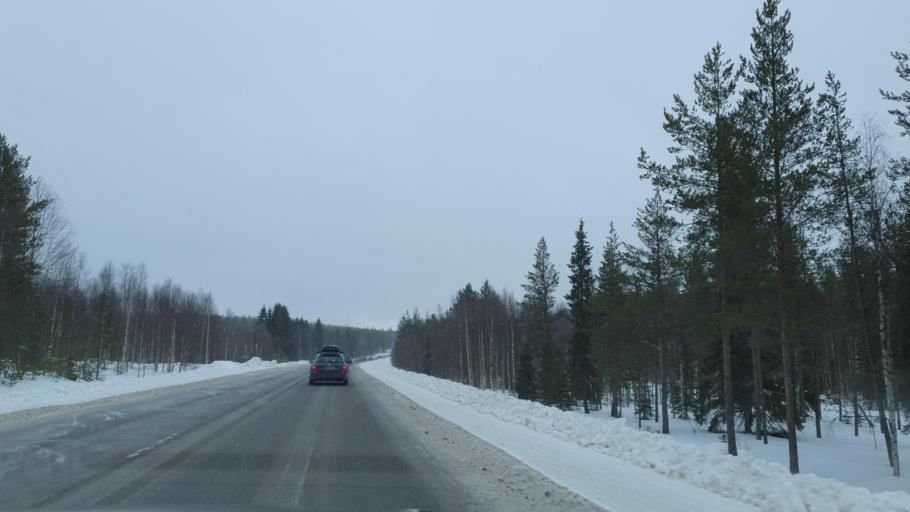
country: FI
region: Lapland
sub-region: Torniolaakso
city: Pello
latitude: 66.9391
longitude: 24.0766
